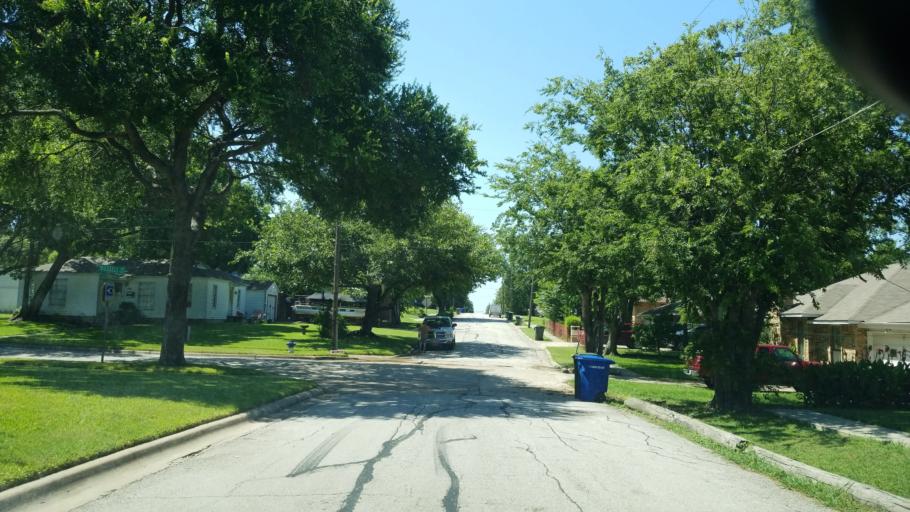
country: US
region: Texas
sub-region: Dallas County
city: Carrollton
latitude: 32.9663
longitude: -96.9108
